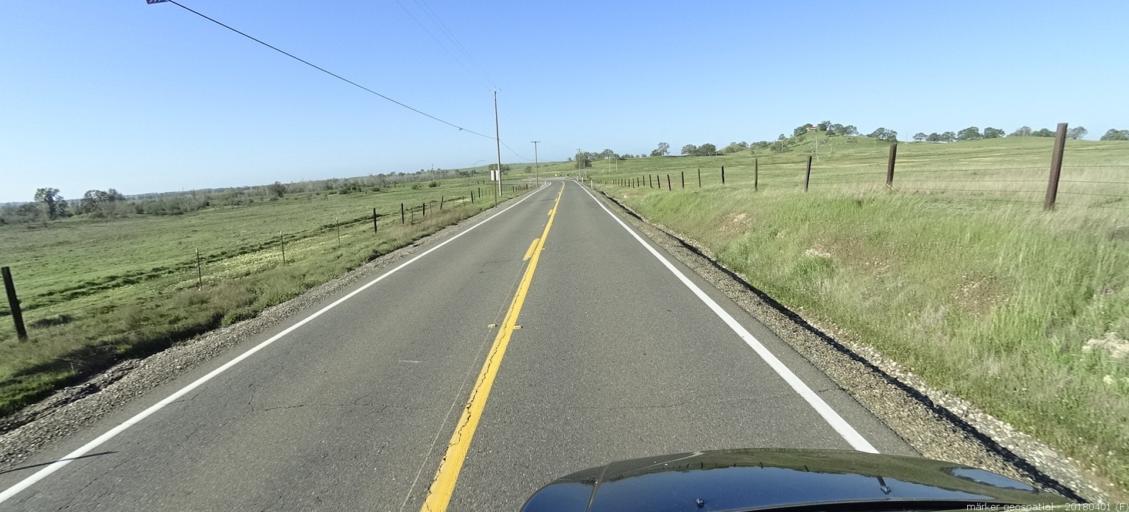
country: US
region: California
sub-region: Sacramento County
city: Rancho Murieta
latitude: 38.4292
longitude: -121.0527
